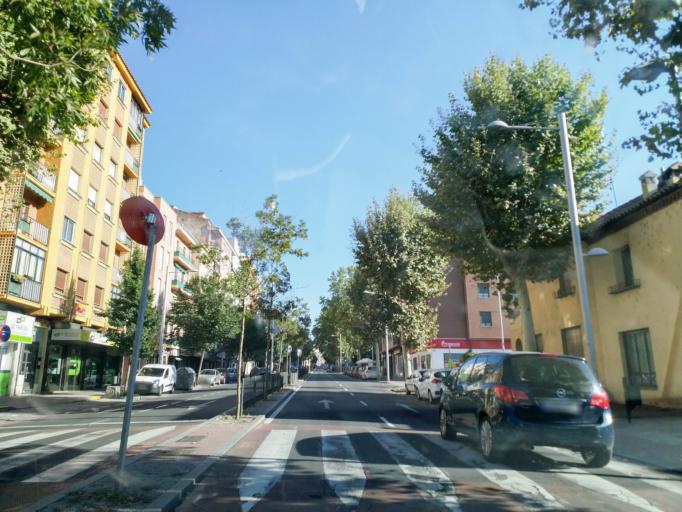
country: ES
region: Castille and Leon
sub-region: Provincia de Segovia
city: Segovia
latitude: 40.9403
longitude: -4.1164
